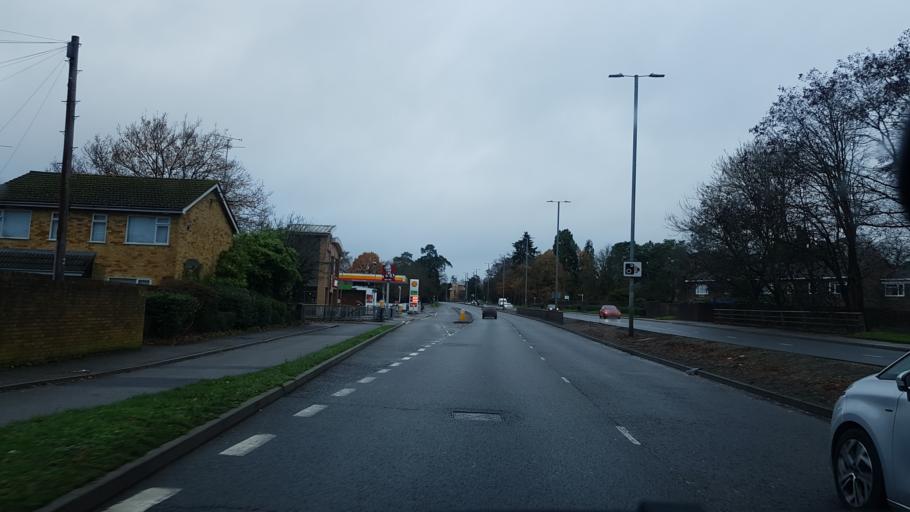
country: GB
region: England
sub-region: Bracknell Forest
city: Bracknell
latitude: 51.4040
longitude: -0.7473
